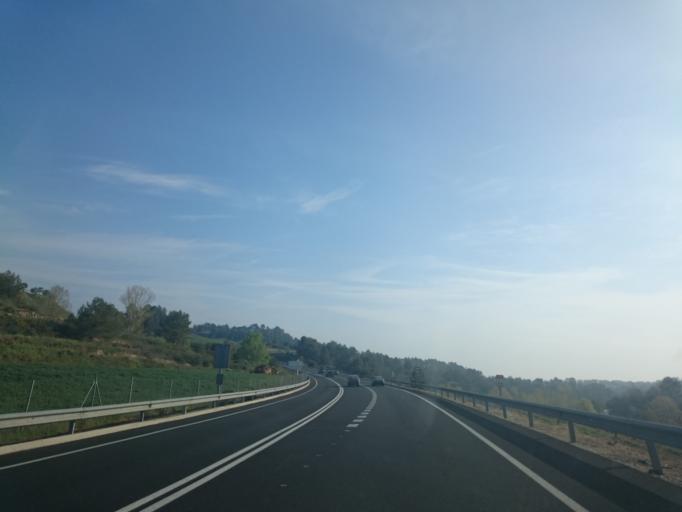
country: ES
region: Catalonia
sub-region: Provincia de Barcelona
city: Sant Salvador de Guardiola
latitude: 41.6730
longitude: 1.7532
